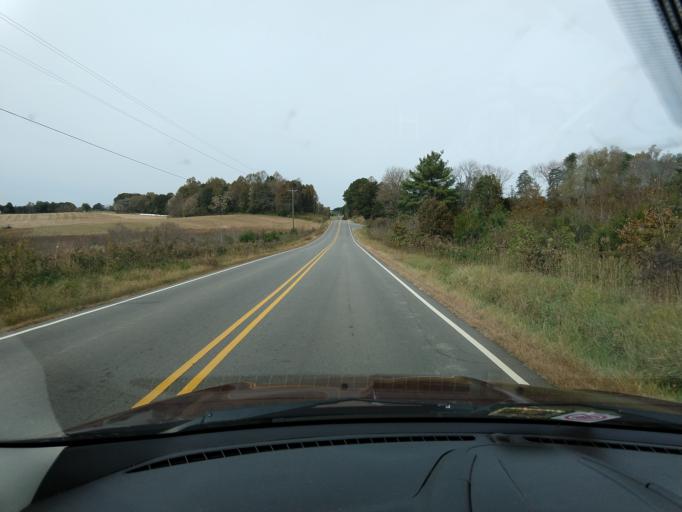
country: US
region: Virginia
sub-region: Franklin County
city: Union Hall
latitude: 36.9598
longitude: -79.5710
